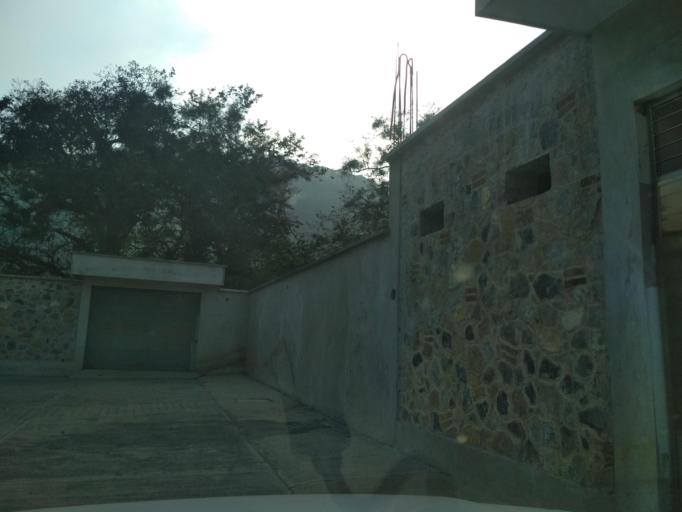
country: MX
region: Veracruz
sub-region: Ixhuatlancillo
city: Fraccionamiento Valle Dorado
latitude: 18.8656
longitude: -97.1176
